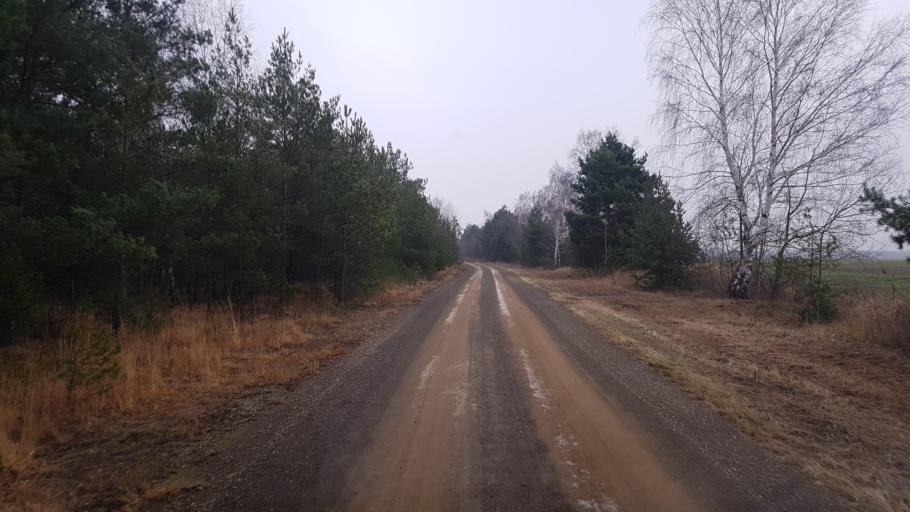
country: DE
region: Brandenburg
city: Plessa
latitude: 51.5122
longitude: 13.6515
